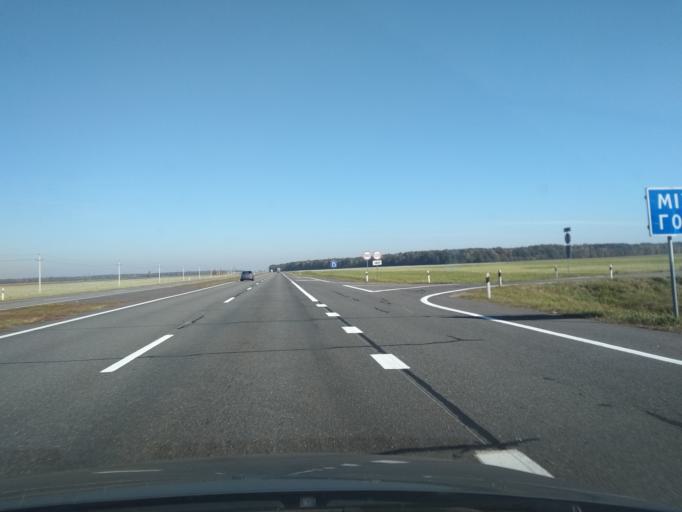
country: BY
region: Brest
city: Antopal'
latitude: 52.3882
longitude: 24.7733
